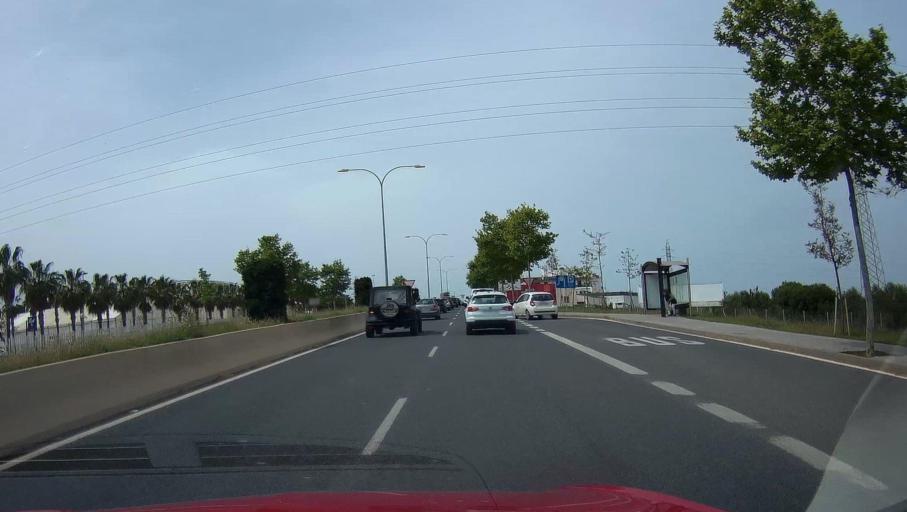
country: ES
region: Balearic Islands
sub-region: Illes Balears
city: Ibiza
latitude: 38.9182
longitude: 1.4268
